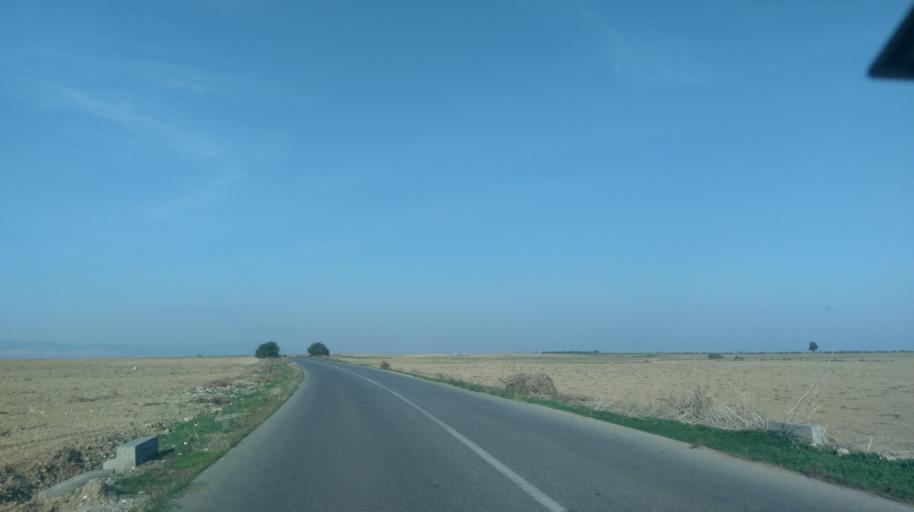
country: CY
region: Ammochostos
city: Achna
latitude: 35.1348
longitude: 33.7408
